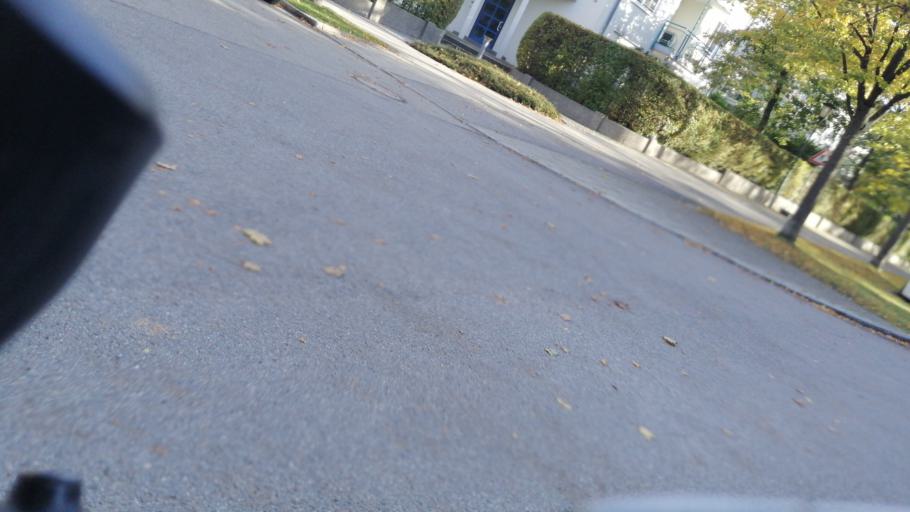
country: DE
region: Bavaria
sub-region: Upper Bavaria
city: Unterfoehring
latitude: 48.2081
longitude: 11.6010
